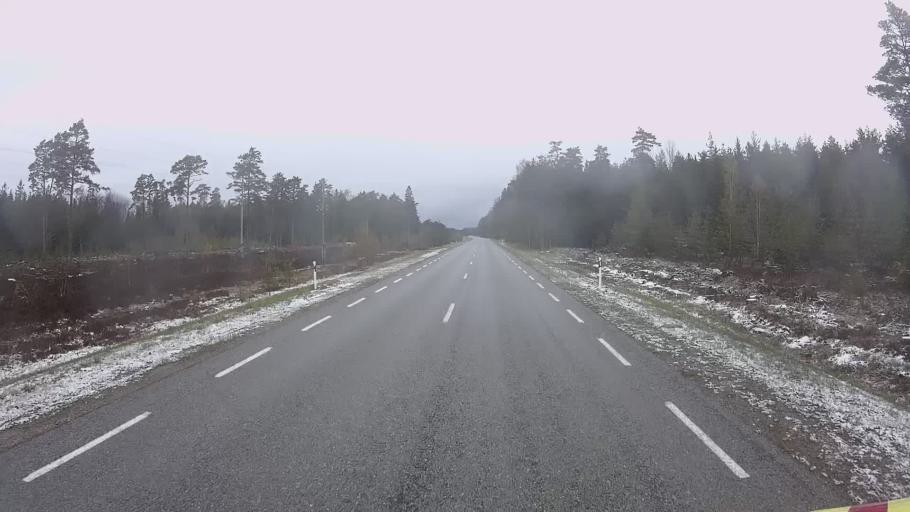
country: EE
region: Hiiumaa
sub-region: Kaerdla linn
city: Kardla
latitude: 59.0154
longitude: 22.6718
